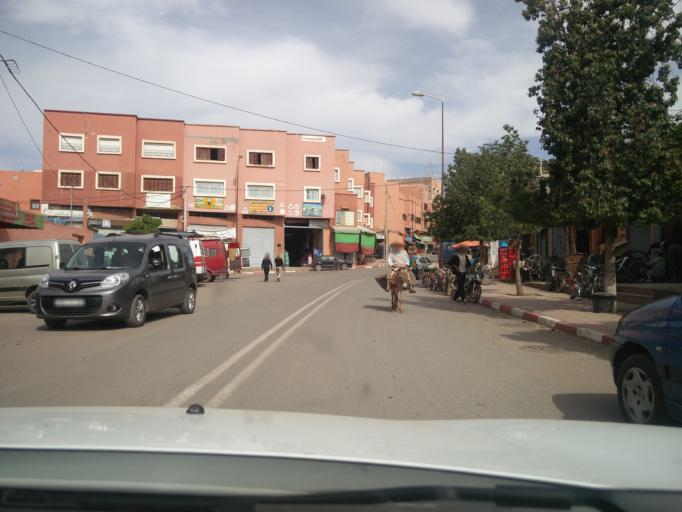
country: MA
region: Tadla-Azilal
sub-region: Azilal Province
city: Demnate
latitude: 31.7331
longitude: -7.0018
